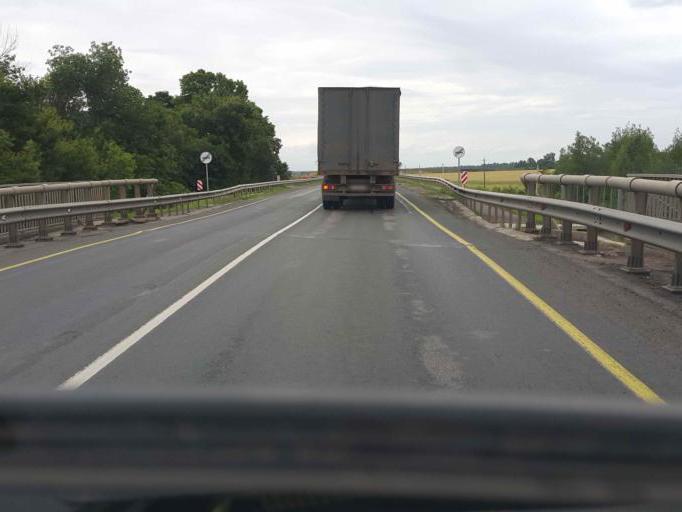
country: RU
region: Tambov
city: Zavoronezhskoye
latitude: 52.9171
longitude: 40.6259
